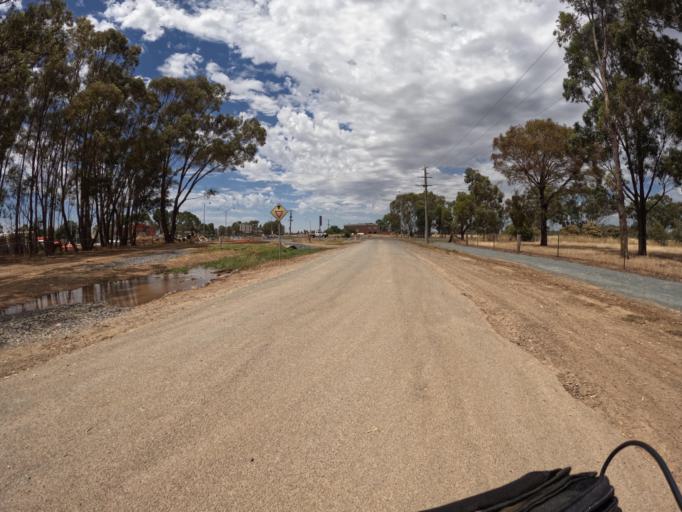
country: AU
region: Victoria
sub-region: Greater Shepparton
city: Shepparton
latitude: -36.6146
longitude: 145.2398
